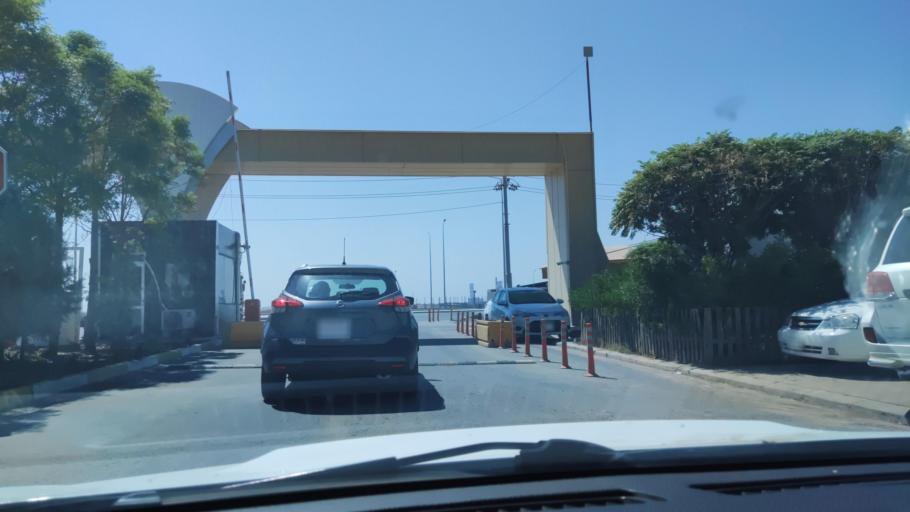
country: IQ
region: Arbil
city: Erbil
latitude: 36.2865
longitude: 44.0494
